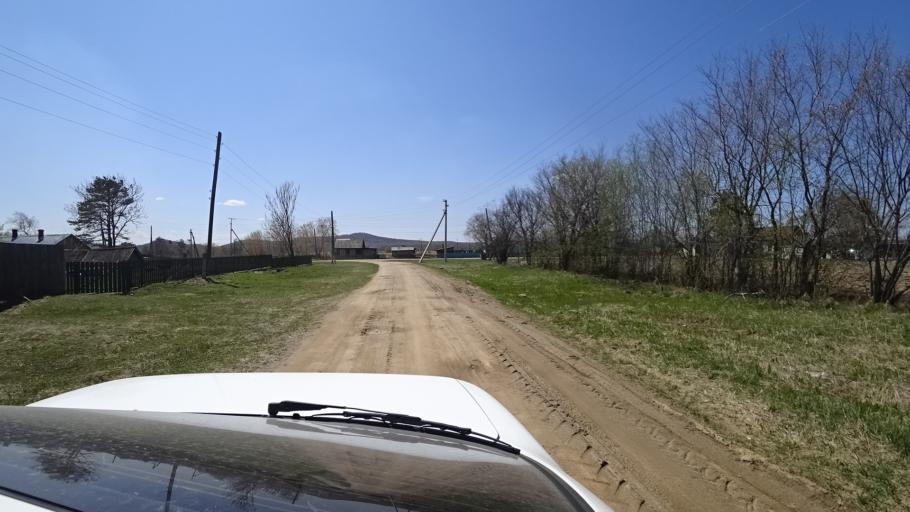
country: RU
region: Primorskiy
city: Dal'nerechensk
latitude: 45.8042
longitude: 133.7649
